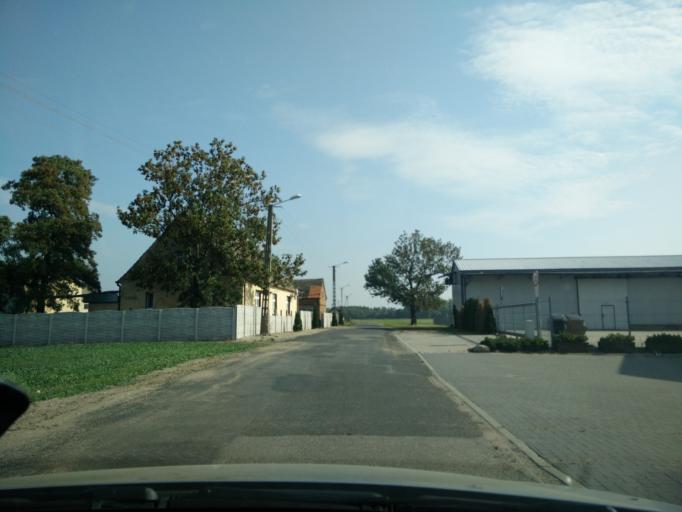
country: PL
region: Greater Poland Voivodeship
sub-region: Powiat poznanski
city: Kleszczewo
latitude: 52.3047
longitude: 17.2459
